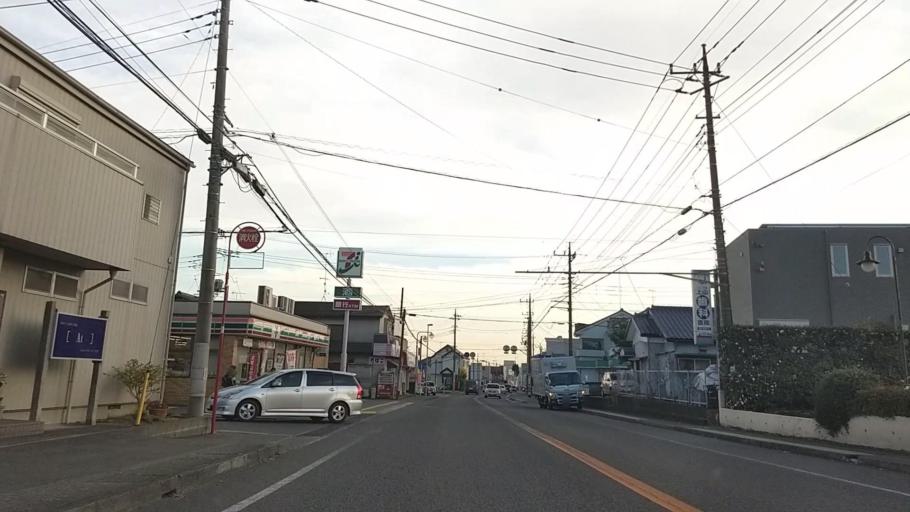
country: JP
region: Kanagawa
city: Atsugi
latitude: 35.4718
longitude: 139.3479
